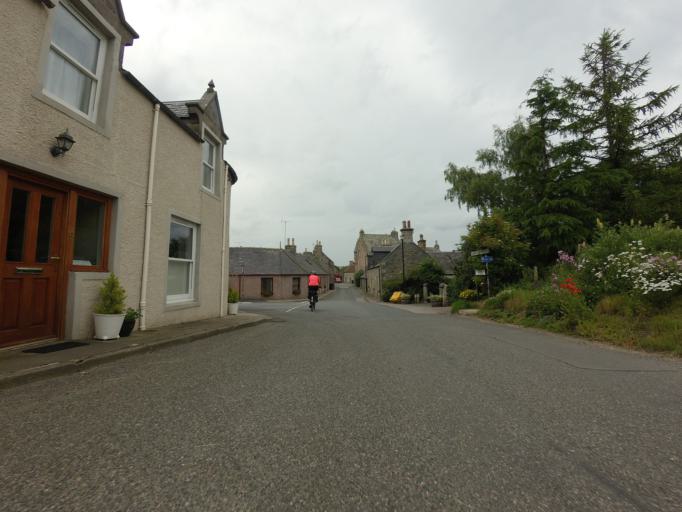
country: GB
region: Scotland
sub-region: Aberdeenshire
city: Portsoy
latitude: 57.6617
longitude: -2.7452
